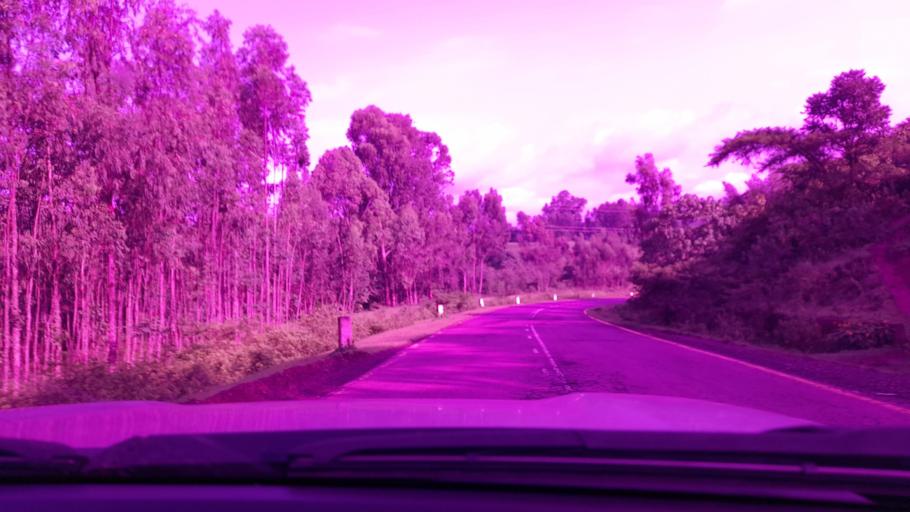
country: ET
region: Oromiya
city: Bedele
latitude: 8.2037
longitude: 36.4400
